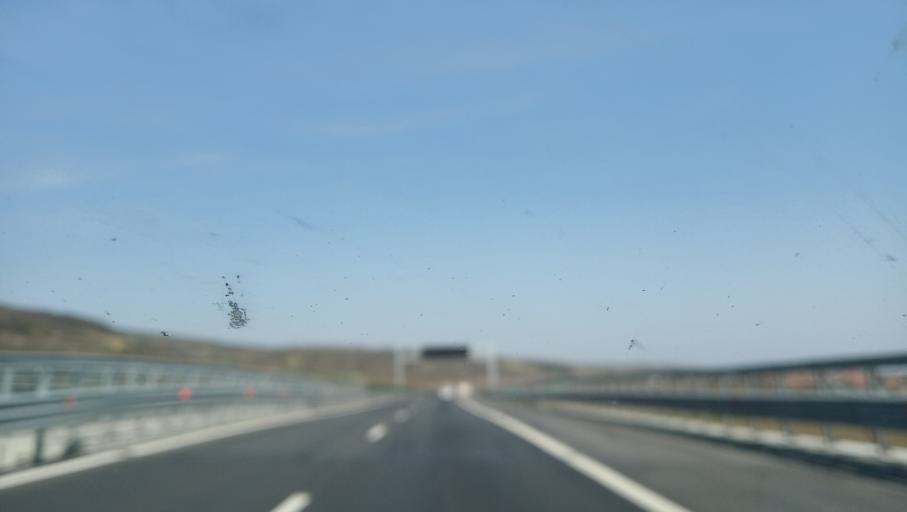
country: RO
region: Alba
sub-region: Comuna Miraslau
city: Miraslau
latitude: 46.3800
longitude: 23.7521
